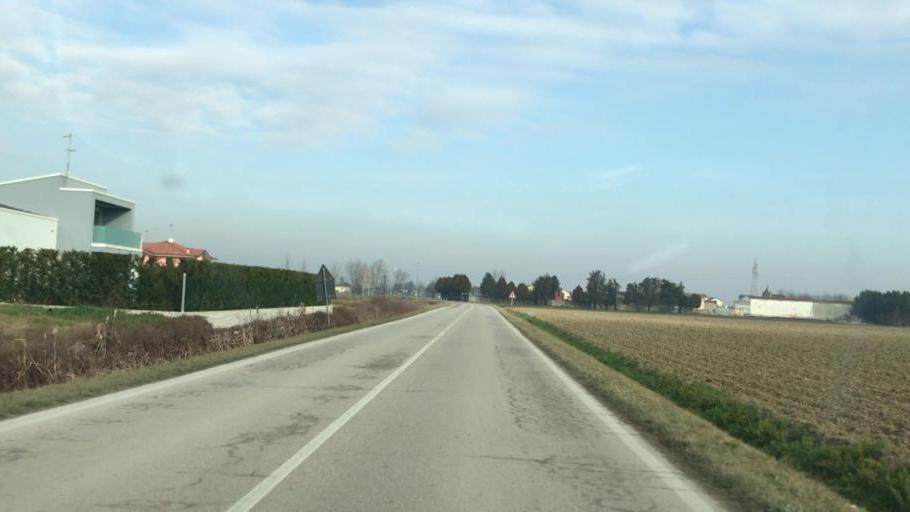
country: IT
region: Veneto
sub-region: Provincia di Rovigo
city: Fratta Polesine
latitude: 45.0314
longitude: 11.6501
